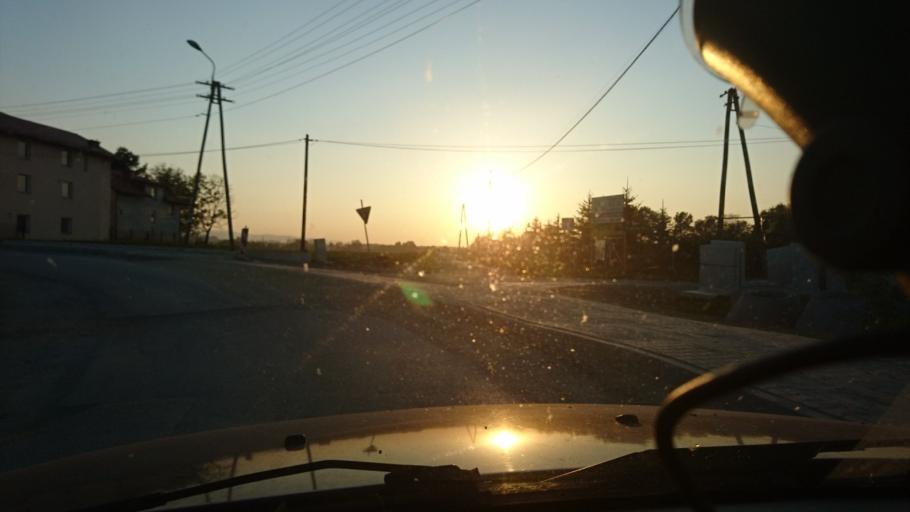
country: PL
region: Silesian Voivodeship
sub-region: Powiat bielski
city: Kozy
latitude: 49.8634
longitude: 19.1340
